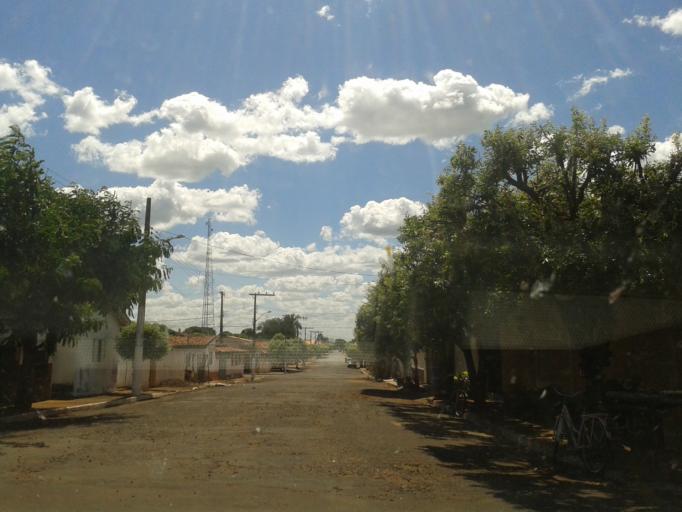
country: BR
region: Minas Gerais
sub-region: Santa Vitoria
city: Santa Vitoria
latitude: -18.6954
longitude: -49.9425
